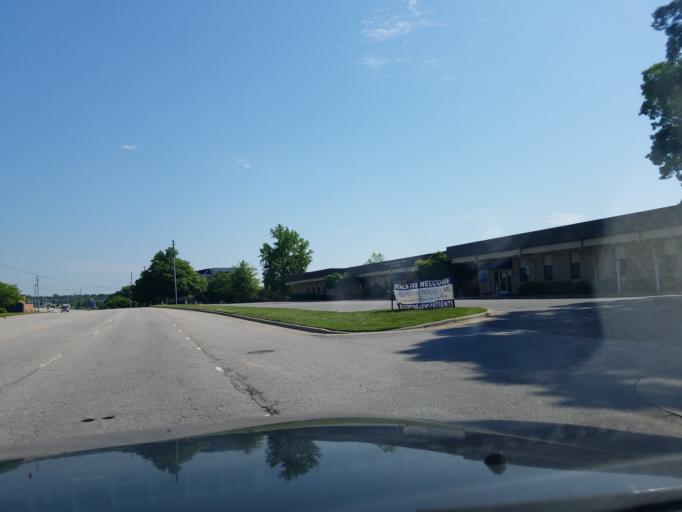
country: US
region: North Carolina
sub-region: Vance County
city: South Henderson
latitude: 36.3308
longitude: -78.4476
